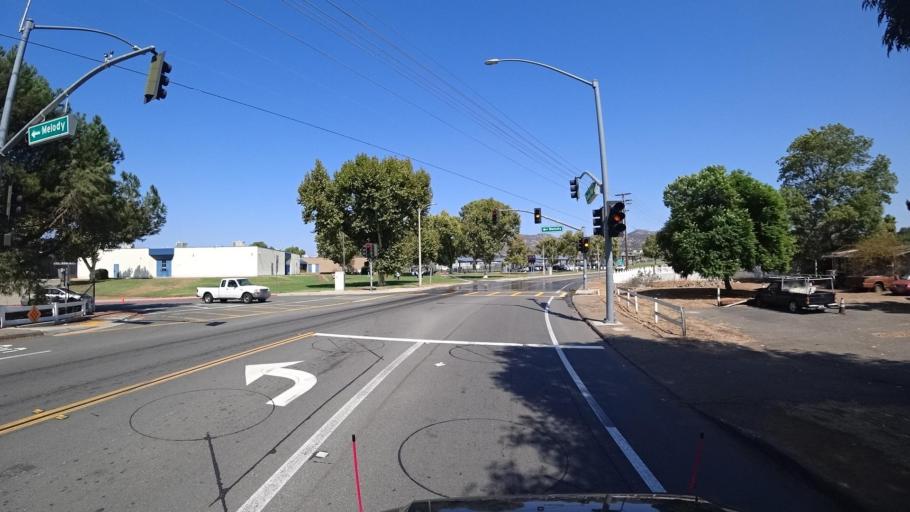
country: US
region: California
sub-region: San Diego County
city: Granite Hills
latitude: 32.7961
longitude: -116.9211
